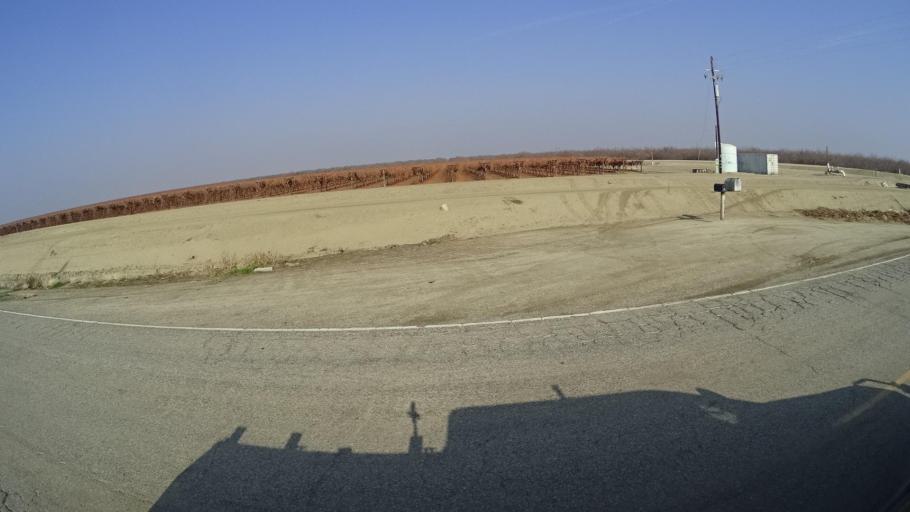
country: US
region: California
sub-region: Kern County
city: Buttonwillow
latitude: 35.3546
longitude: -119.3838
